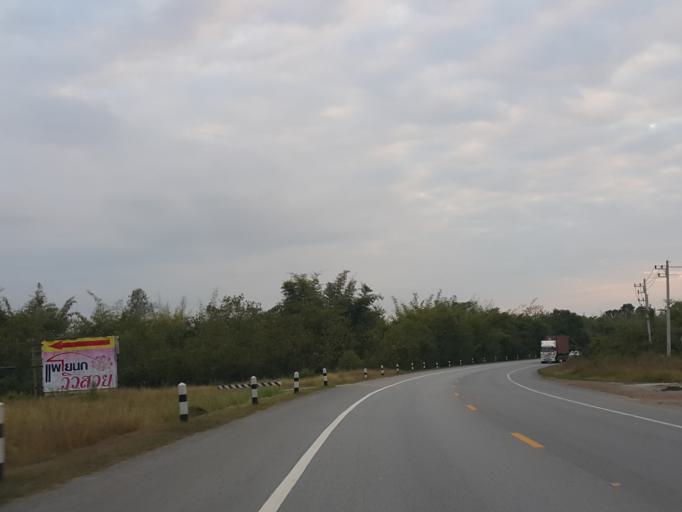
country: TH
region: Lampang
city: Lampang
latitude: 18.2530
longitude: 99.5389
